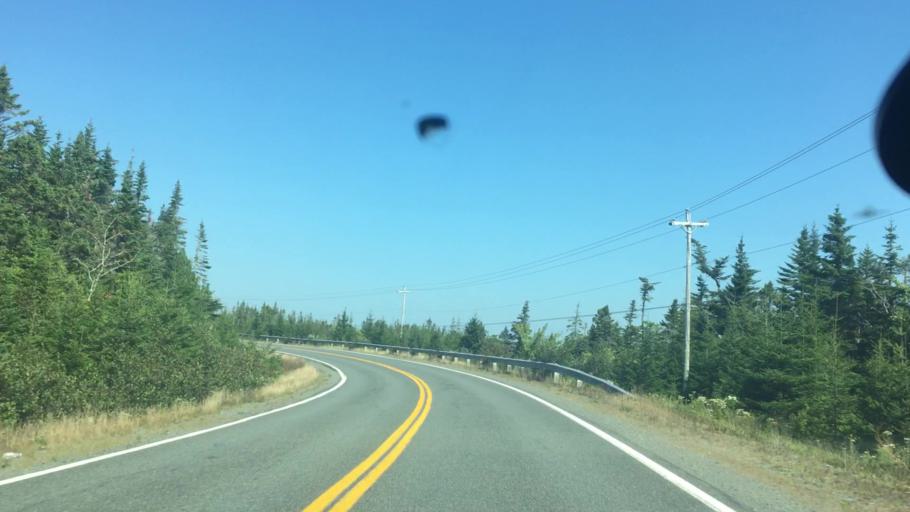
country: CA
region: Nova Scotia
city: Antigonish
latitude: 44.9890
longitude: -62.0958
